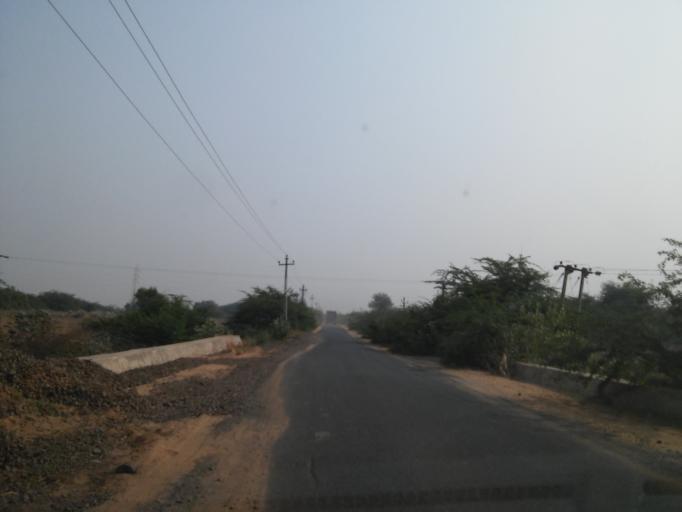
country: IN
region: Gujarat
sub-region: Kachchh
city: Bhuj
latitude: 23.4294
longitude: 69.6833
